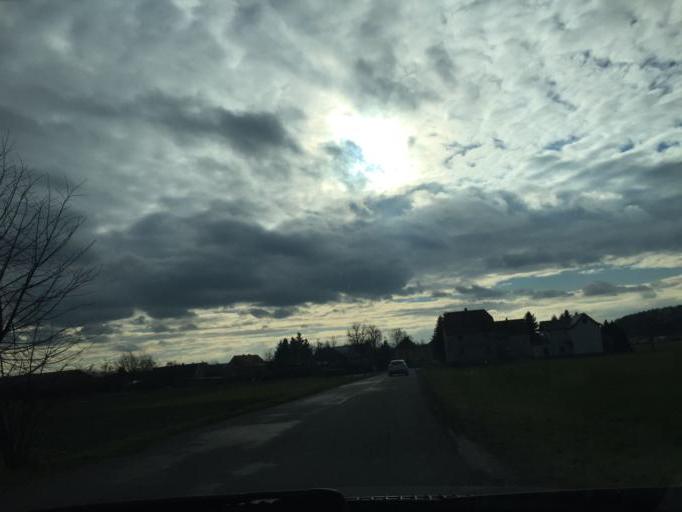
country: DE
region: Saxony
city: Ebersbach
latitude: 51.2052
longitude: 13.6715
